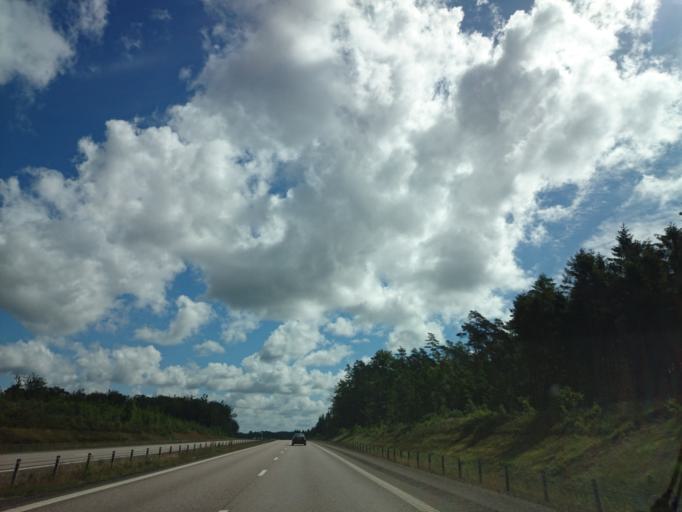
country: SE
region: Skane
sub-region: Orkelljunga Kommun
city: OErkelljunga
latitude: 56.2613
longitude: 13.2966
